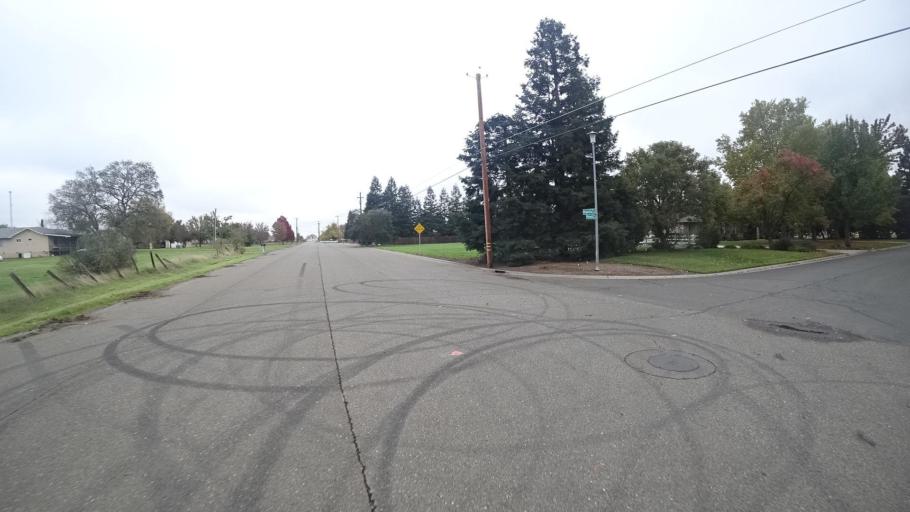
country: US
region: California
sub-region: Sacramento County
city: Wilton
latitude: 38.4473
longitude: -121.2949
